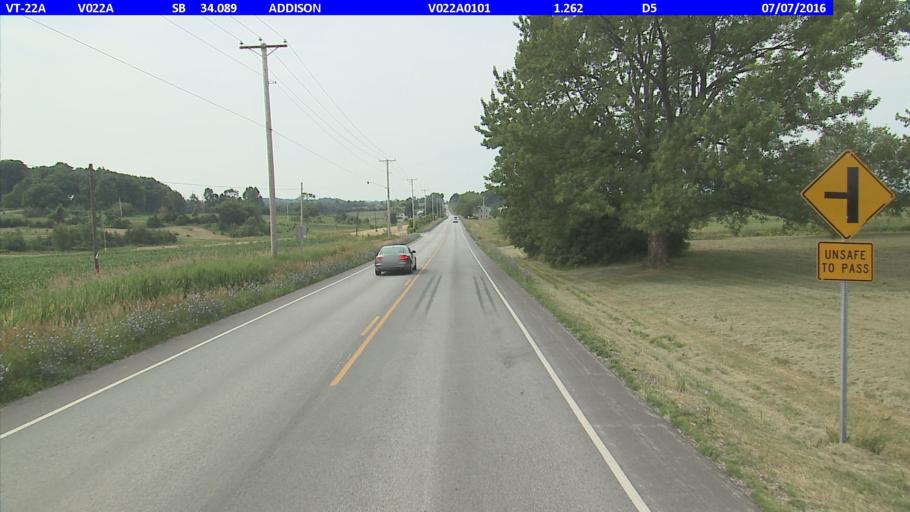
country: US
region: Vermont
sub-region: Addison County
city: Vergennes
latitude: 44.0478
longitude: -73.3030
